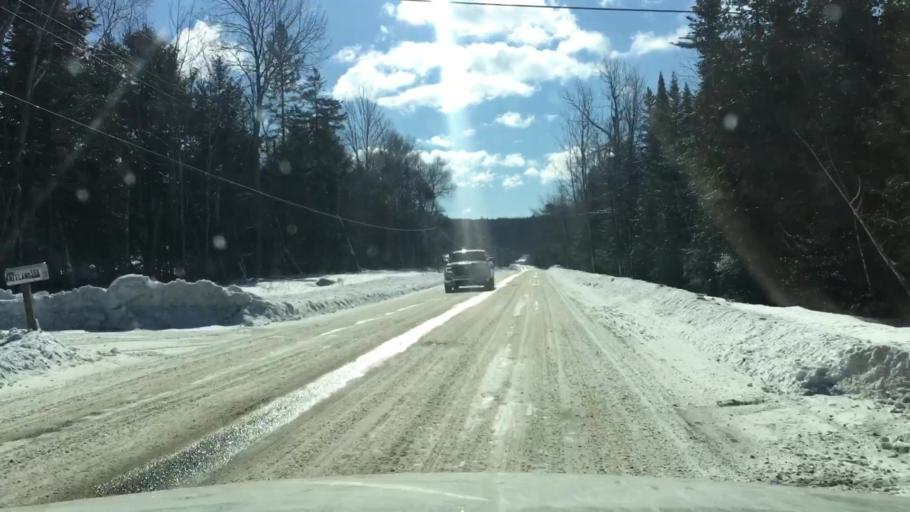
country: US
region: Maine
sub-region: Washington County
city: Calais
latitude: 45.0682
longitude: -67.4743
